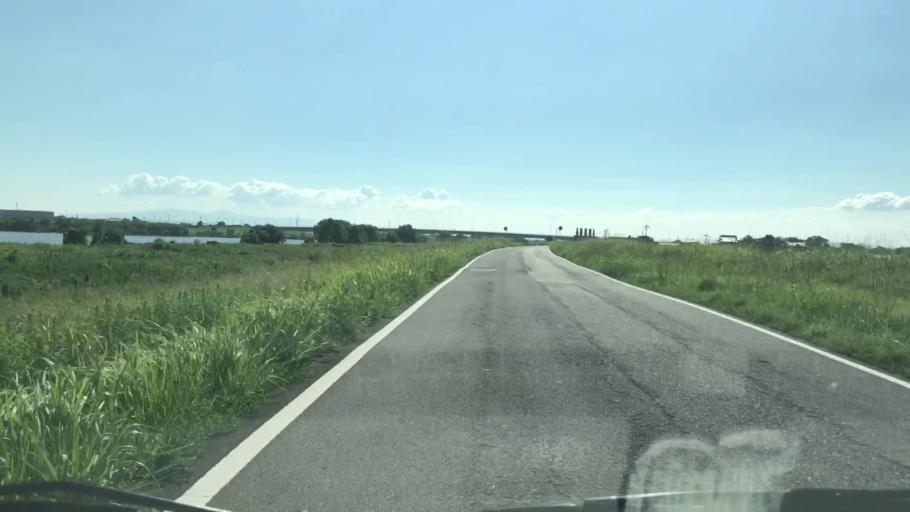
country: JP
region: Saga Prefecture
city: Kanzakimachi-kanzaki
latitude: 33.2742
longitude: 130.4399
